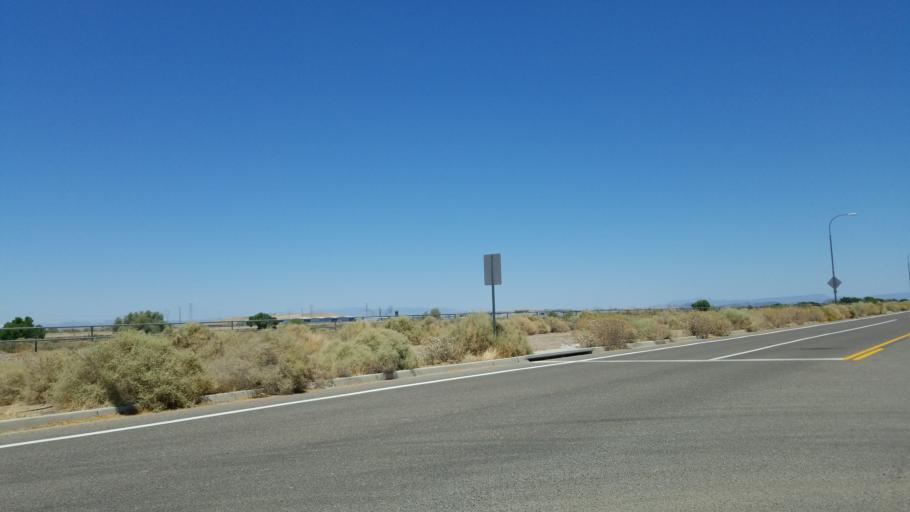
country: US
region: Arizona
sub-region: Maricopa County
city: Litchfield Park
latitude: 33.5142
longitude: -112.2986
